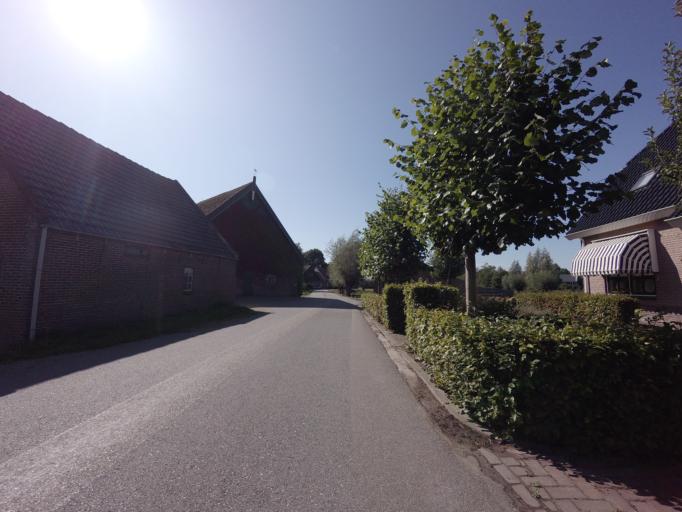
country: NL
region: South Holland
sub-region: Gemeente Giessenlanden
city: Giessenburg
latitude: 51.8695
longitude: 4.9128
